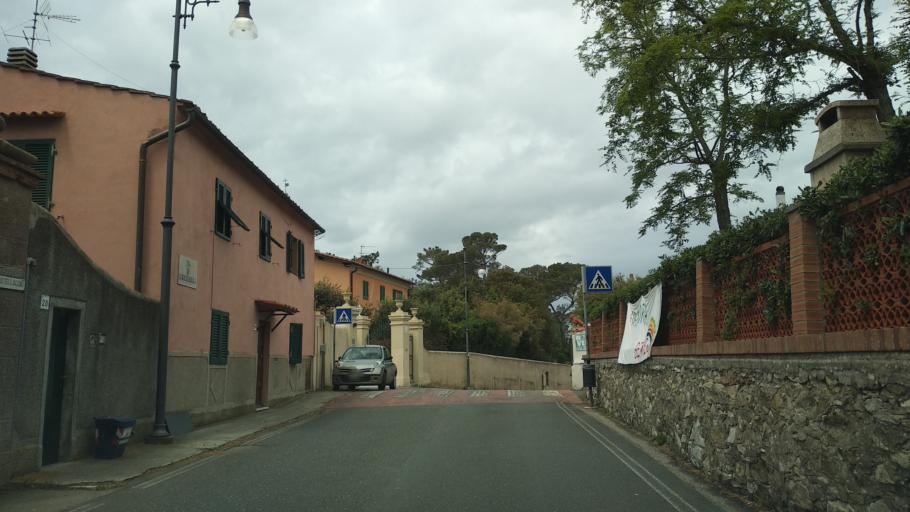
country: IT
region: Tuscany
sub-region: Provincia di Livorno
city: Quercianella
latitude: 43.4903
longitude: 10.3589
